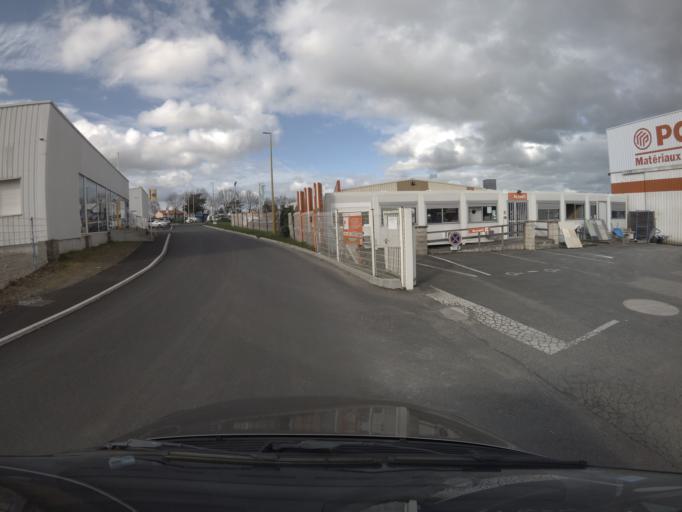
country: FR
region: Pays de la Loire
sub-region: Departement de la Vendee
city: Montaigu
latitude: 46.9720
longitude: -1.3242
